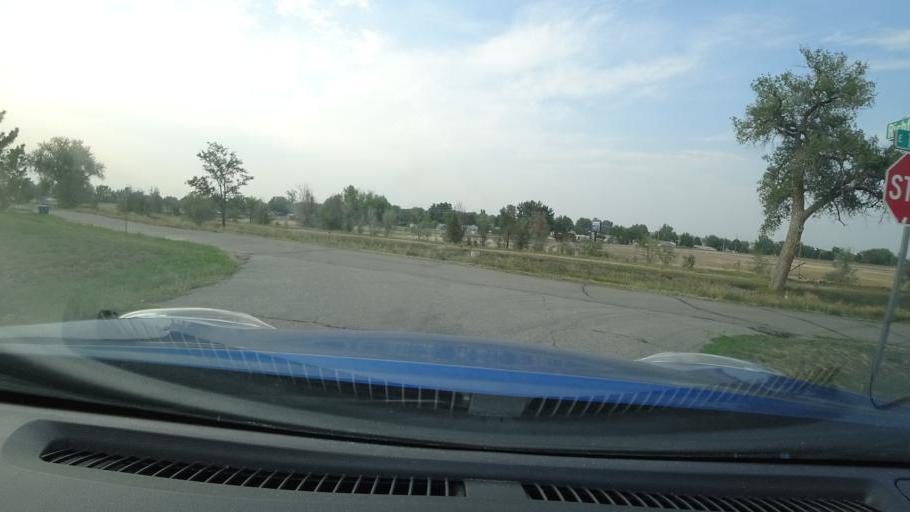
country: US
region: Colorado
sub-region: Adams County
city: Aurora
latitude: 39.7386
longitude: -104.7865
